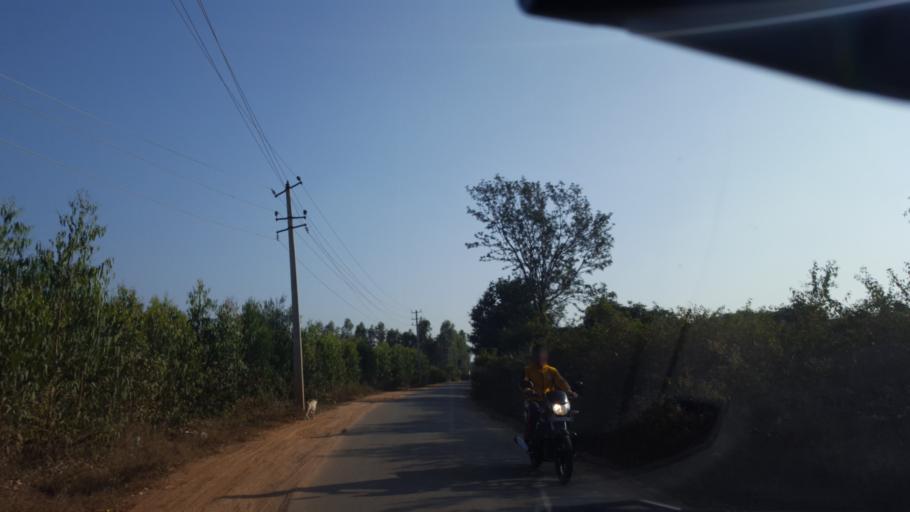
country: IN
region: Karnataka
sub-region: Bangalore Rural
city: Hoskote
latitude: 12.9225
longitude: 77.7567
